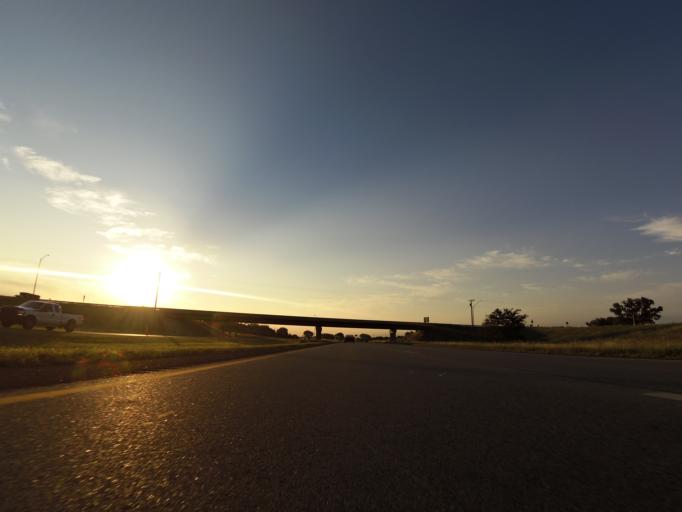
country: US
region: Kansas
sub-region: Sedgwick County
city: Maize
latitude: 37.7567
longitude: -97.3913
